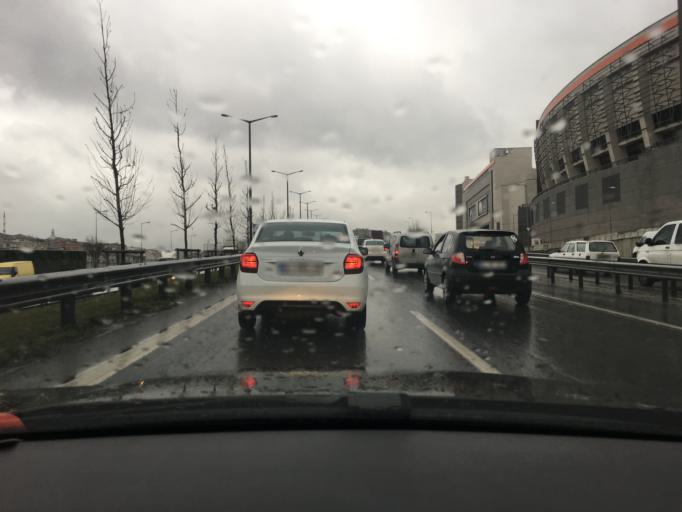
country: TR
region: Istanbul
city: Esenler
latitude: 41.0408
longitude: 28.8866
